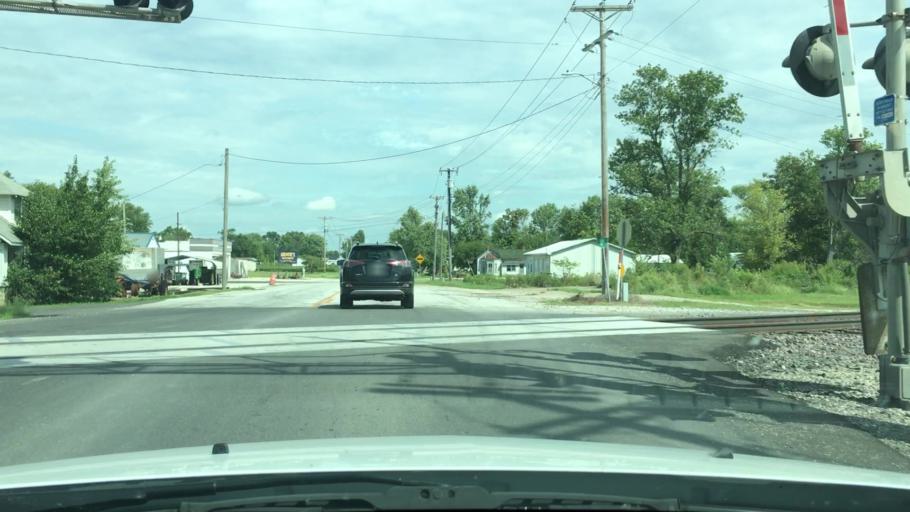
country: US
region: Missouri
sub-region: Audrain County
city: Vandalia
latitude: 39.2424
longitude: -91.6455
